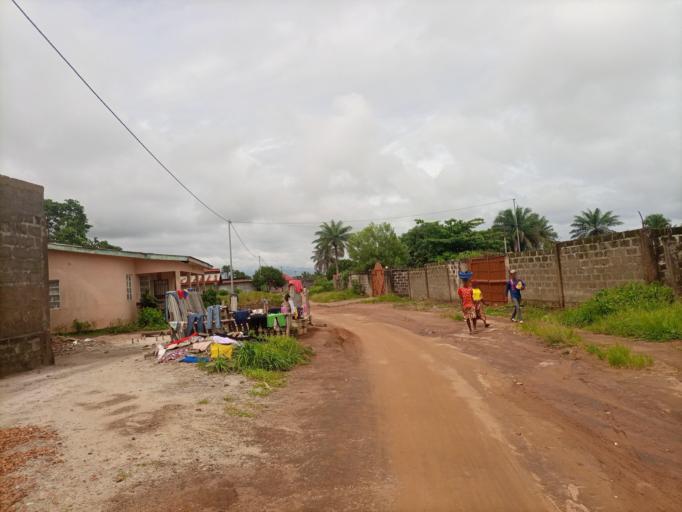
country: SL
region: Northern Province
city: Masoyila
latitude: 8.5993
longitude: -13.1760
